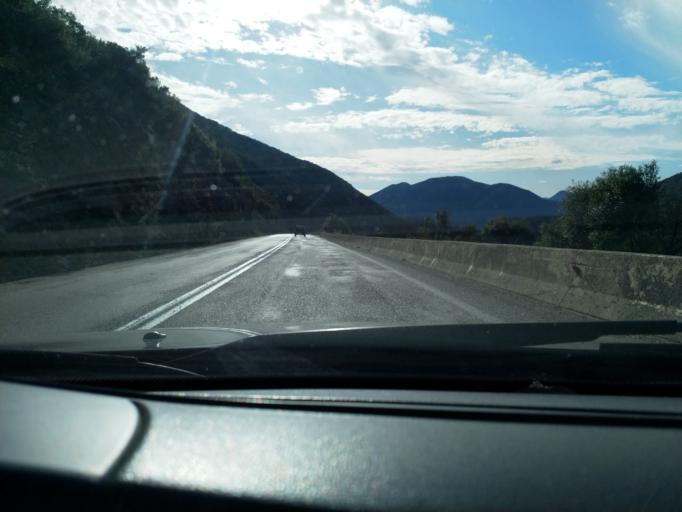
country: GR
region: Epirus
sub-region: Nomos Ioanninon
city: Agia Kyriaki
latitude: 39.4924
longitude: 20.8743
